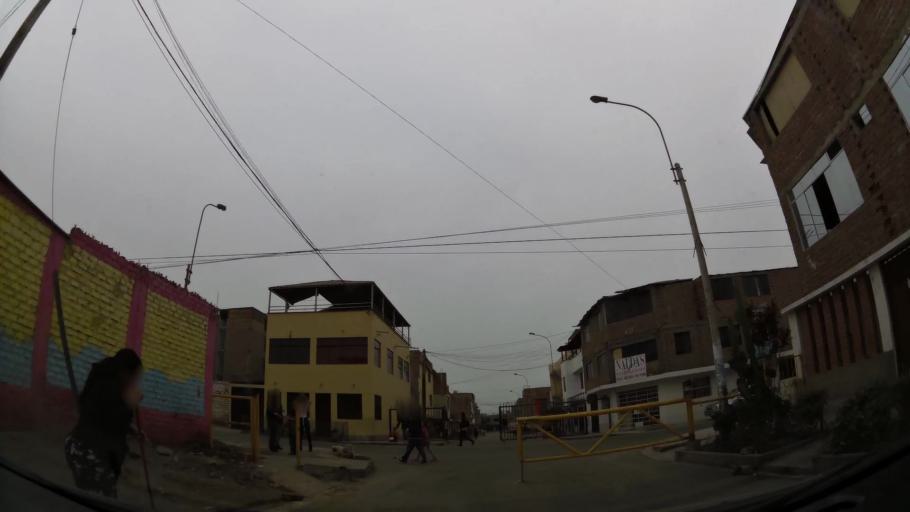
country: PE
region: Lima
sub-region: Lima
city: Surco
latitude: -12.1810
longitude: -76.9802
